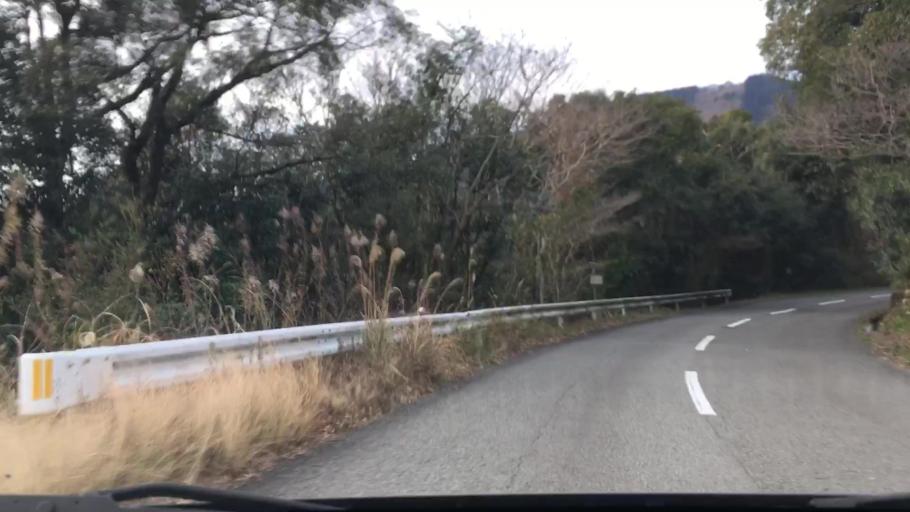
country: JP
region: Miyazaki
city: Nichinan
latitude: 31.6610
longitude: 131.3173
